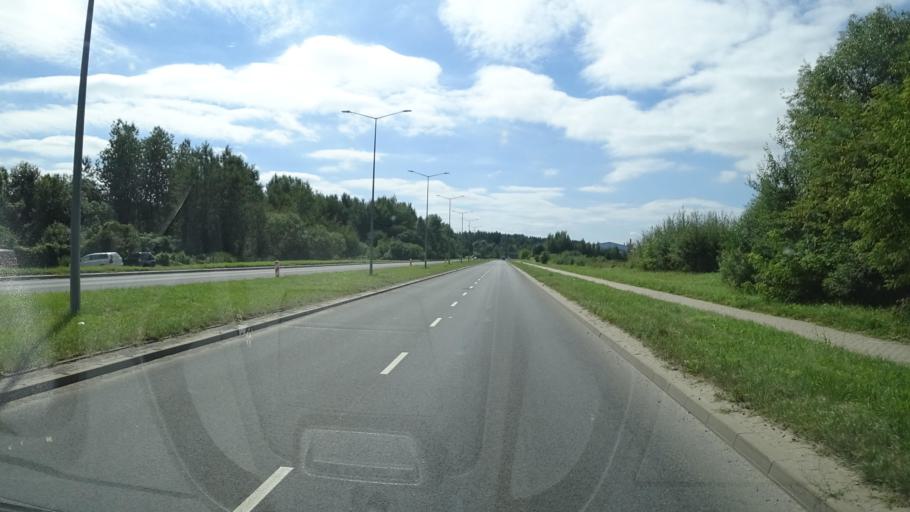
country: PL
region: Warmian-Masurian Voivodeship
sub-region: Powiat elcki
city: Elk
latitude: 53.8237
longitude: 22.3902
